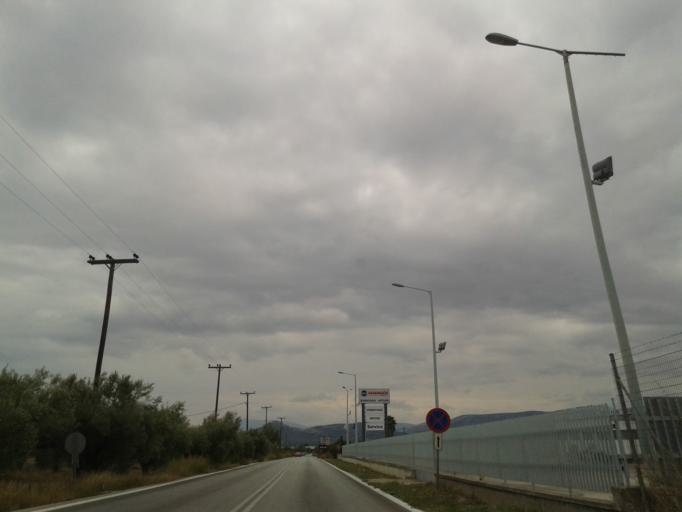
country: GR
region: Peloponnese
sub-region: Nomos Argolidos
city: Koutsopodi
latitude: 37.7062
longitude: 22.7242
